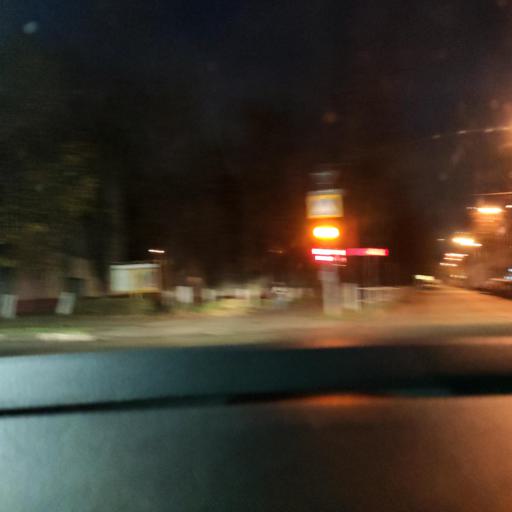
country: RU
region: Moskovskaya
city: Reutov
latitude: 55.7623
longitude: 37.8569
